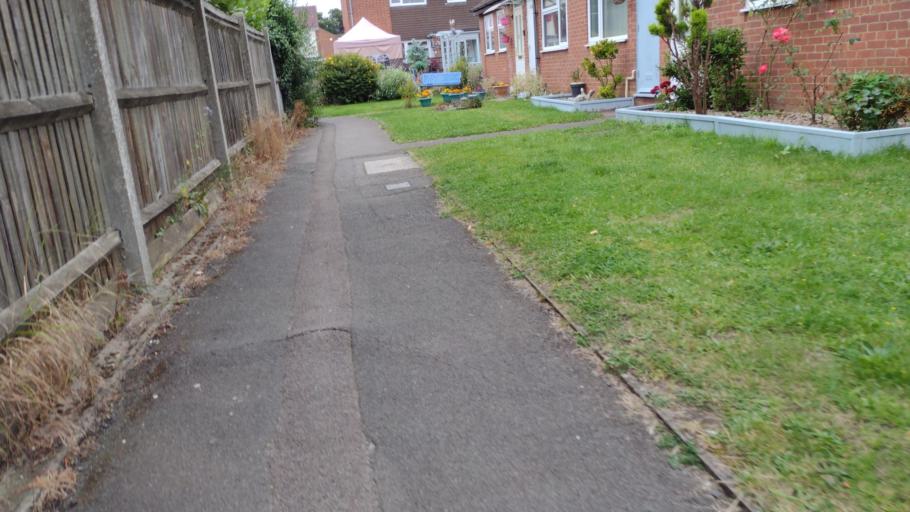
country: GB
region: England
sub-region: Wokingham
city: Winnersh
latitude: 51.4323
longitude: -0.8861
